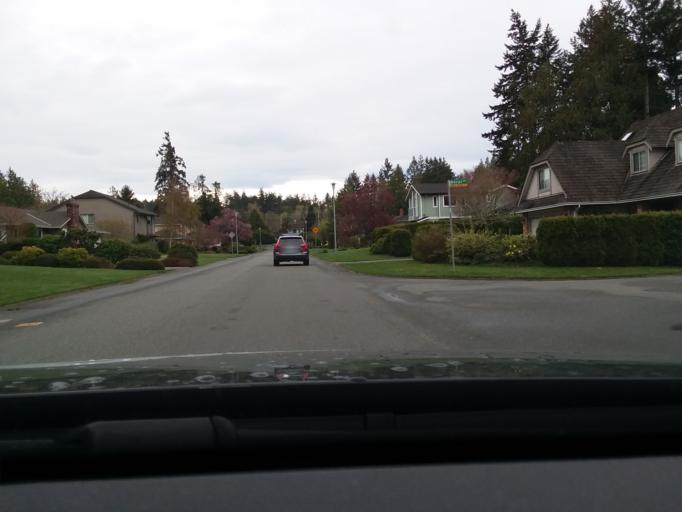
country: CA
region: British Columbia
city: Victoria
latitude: 48.5163
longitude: -123.3785
